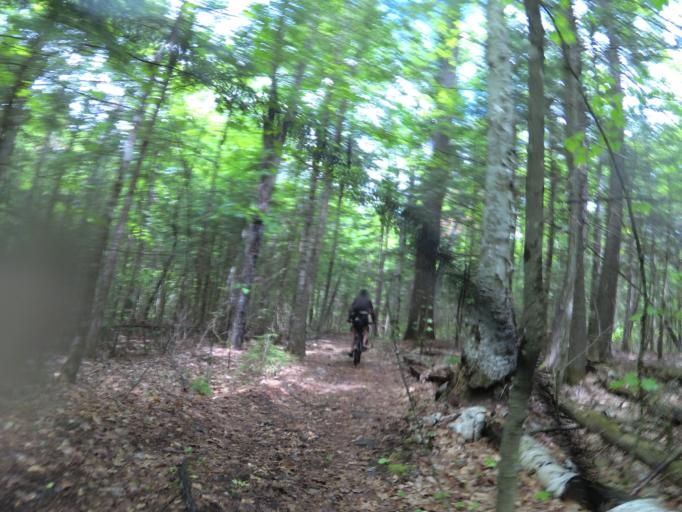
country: CA
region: Ontario
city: Renfrew
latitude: 45.0820
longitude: -76.8927
